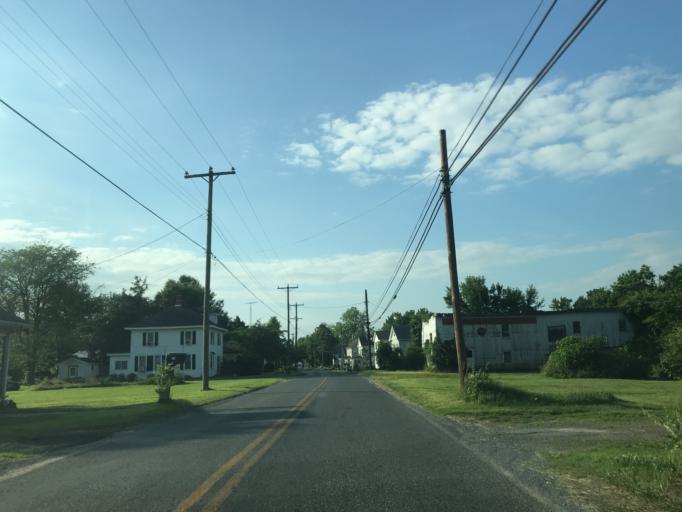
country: US
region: Maryland
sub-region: Caroline County
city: Federalsburg
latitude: 38.7043
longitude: -75.7763
